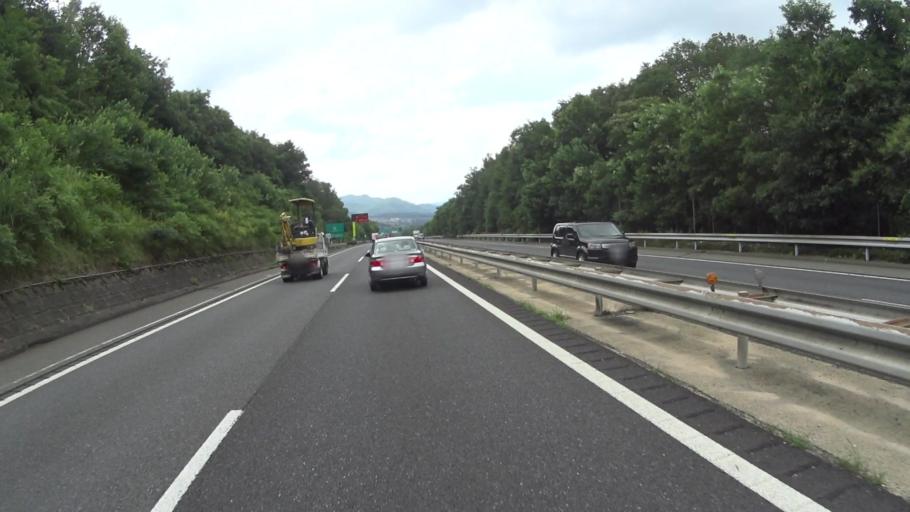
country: JP
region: Kyoto
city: Kameoka
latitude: 34.9902
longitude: 135.6154
